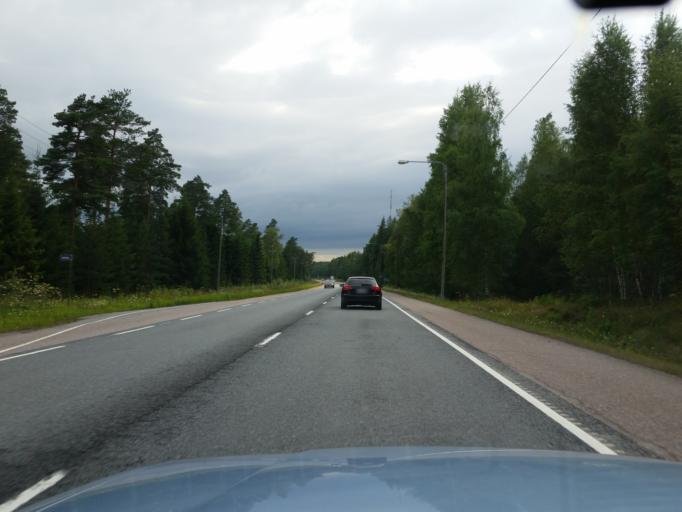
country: FI
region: Uusimaa
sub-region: Raaseporin
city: Ekenaes
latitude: 59.9998
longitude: 23.5151
